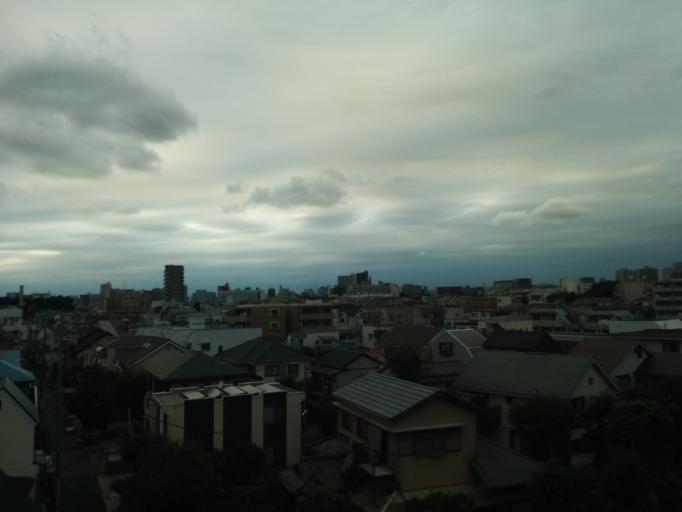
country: JP
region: Tokyo
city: Tokyo
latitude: 35.6130
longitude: 139.7280
